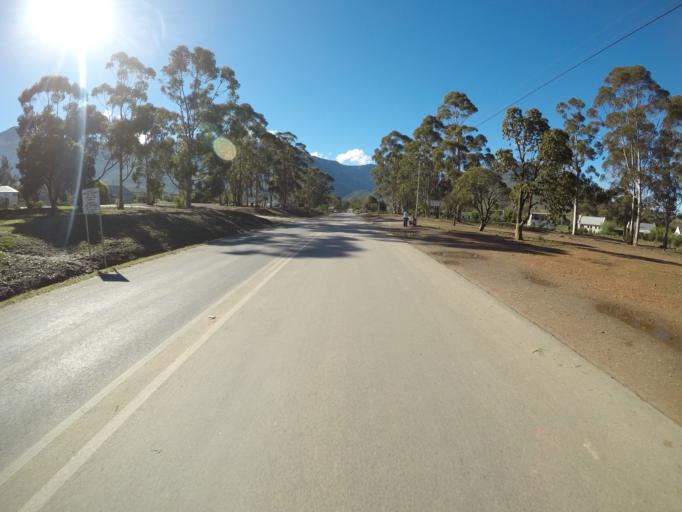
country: ZA
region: Western Cape
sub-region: Overberg District Municipality
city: Caledon
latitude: -34.0547
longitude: 19.6023
